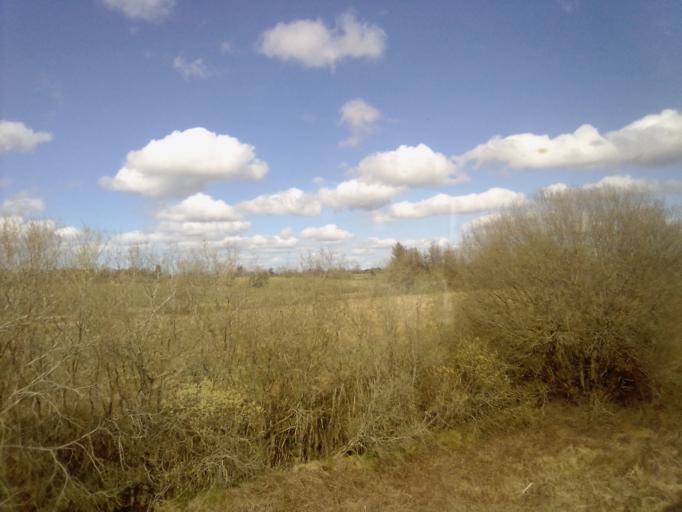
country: IE
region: Munster
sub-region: County Cork
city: Millstreet
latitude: 52.0856
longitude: -9.2221
